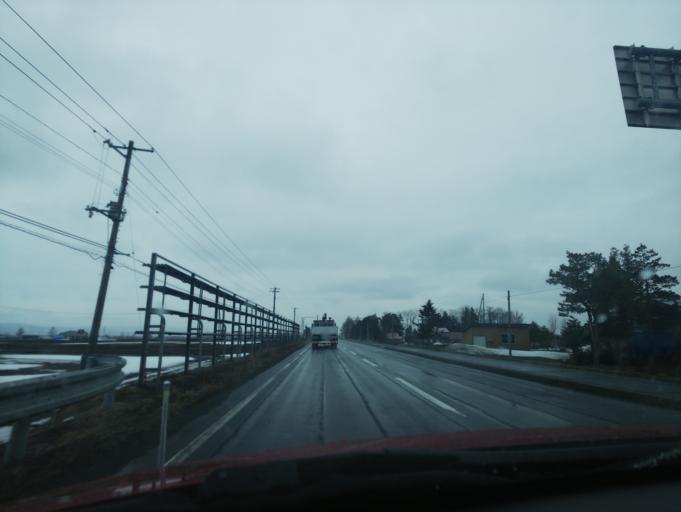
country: JP
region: Hokkaido
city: Nayoro
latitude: 44.2174
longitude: 142.3948
